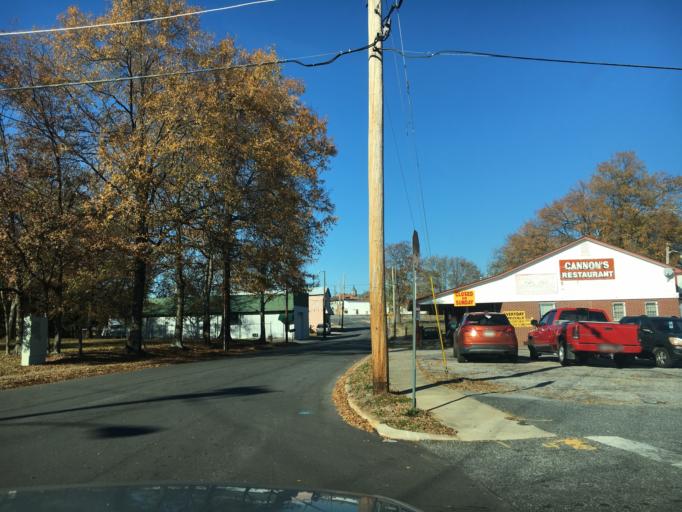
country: US
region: South Carolina
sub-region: Greenville County
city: Greer
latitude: 34.9335
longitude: -82.2257
